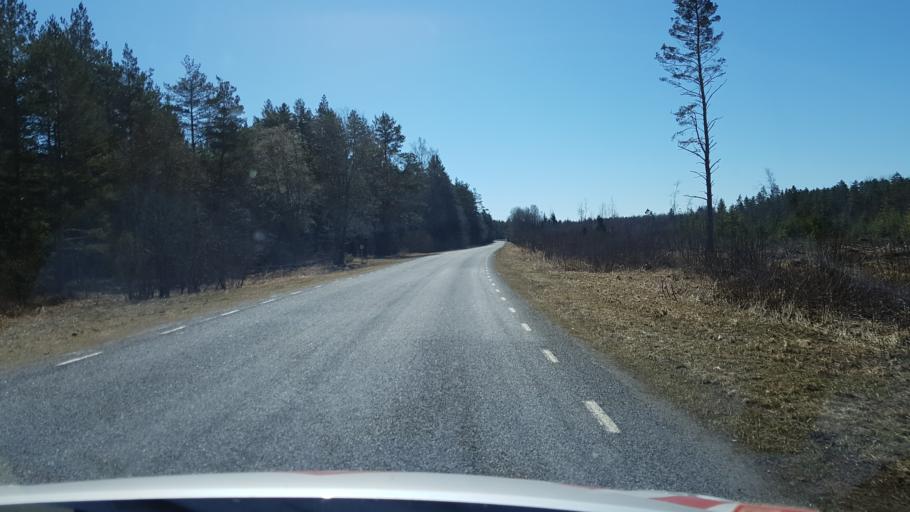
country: EE
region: Laeaene-Virumaa
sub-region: Haljala vald
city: Haljala
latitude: 59.5065
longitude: 26.2376
